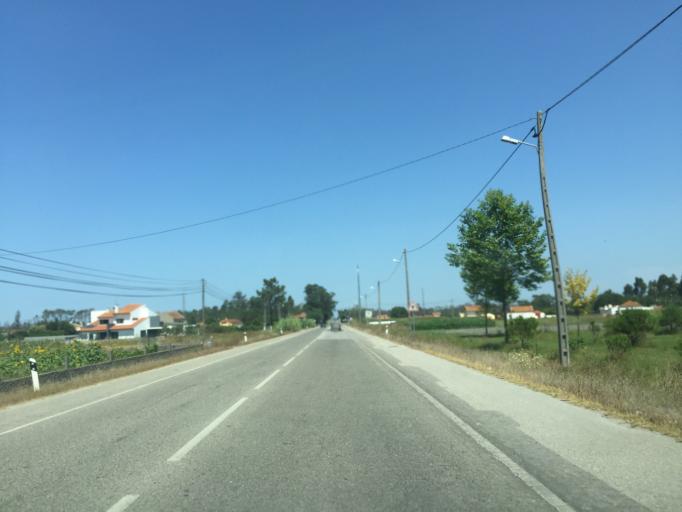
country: PT
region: Coimbra
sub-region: Mira
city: Mira
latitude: 40.3264
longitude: -8.7516
